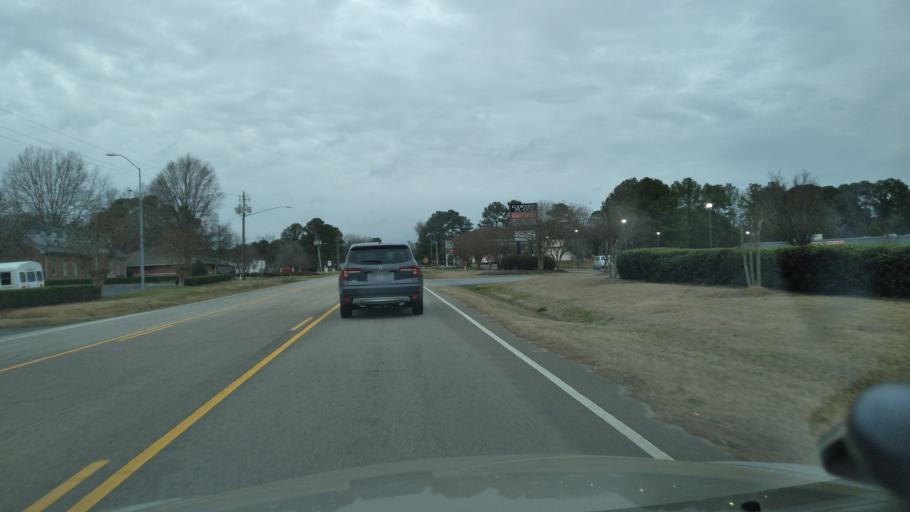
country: US
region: North Carolina
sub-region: Wake County
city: Garner
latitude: 35.7037
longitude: -78.6128
